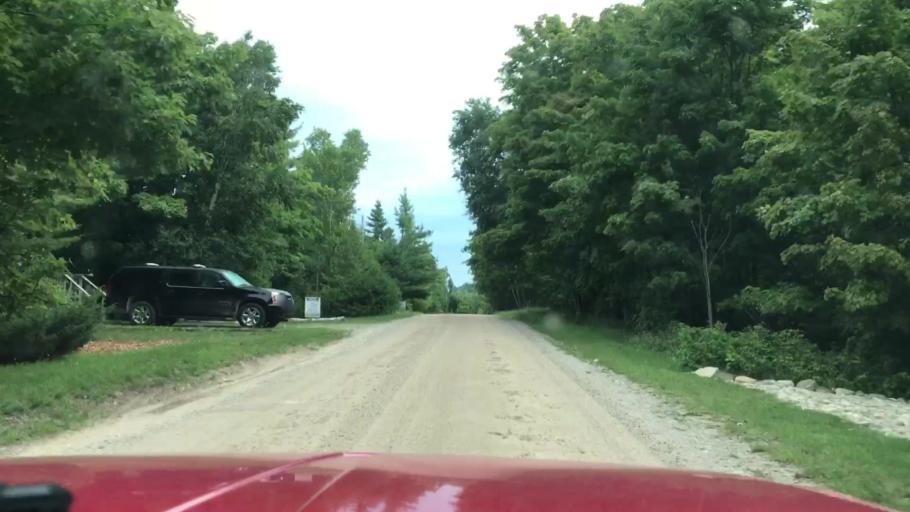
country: US
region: Michigan
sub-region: Charlevoix County
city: Charlevoix
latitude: 45.7299
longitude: -85.5651
